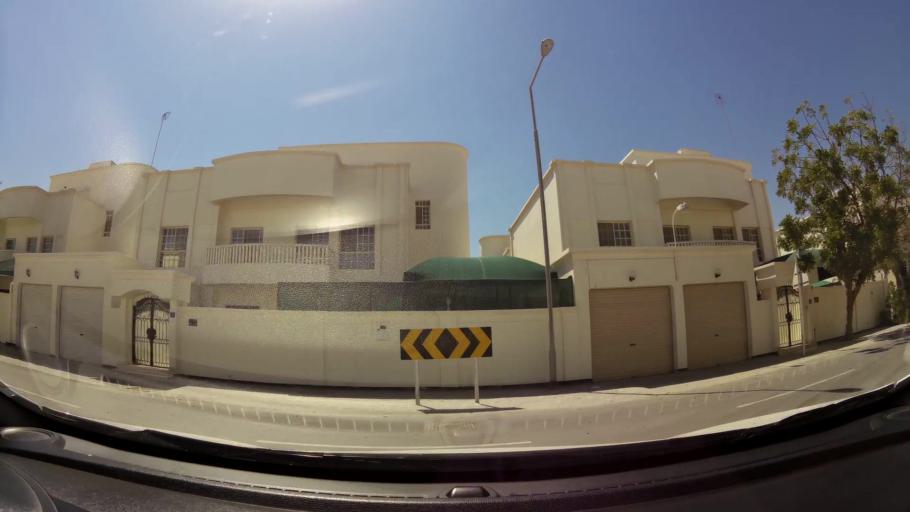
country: BH
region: Muharraq
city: Al Muharraq
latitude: 26.2791
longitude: 50.6023
